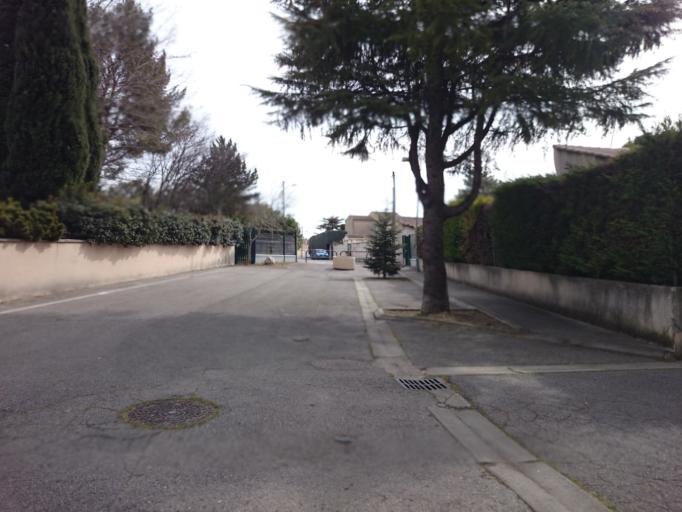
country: FR
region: Provence-Alpes-Cote d'Azur
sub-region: Departement du Vaucluse
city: Vedene
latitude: 43.9824
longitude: 4.9121
